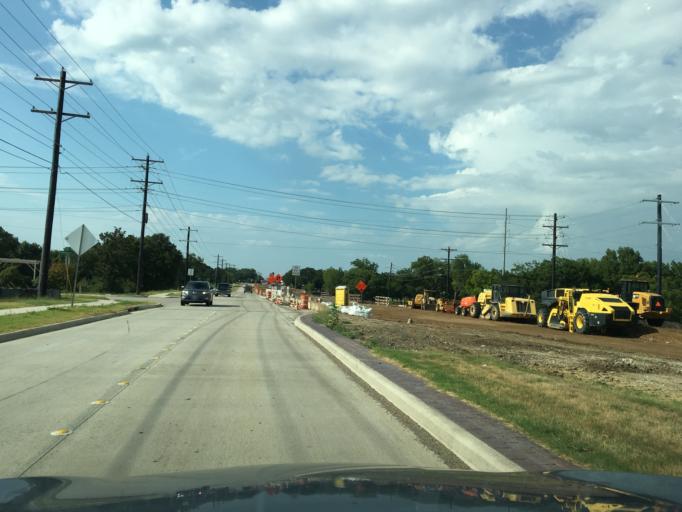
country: US
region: Texas
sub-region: Denton County
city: Denton
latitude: 33.2271
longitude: -97.0831
